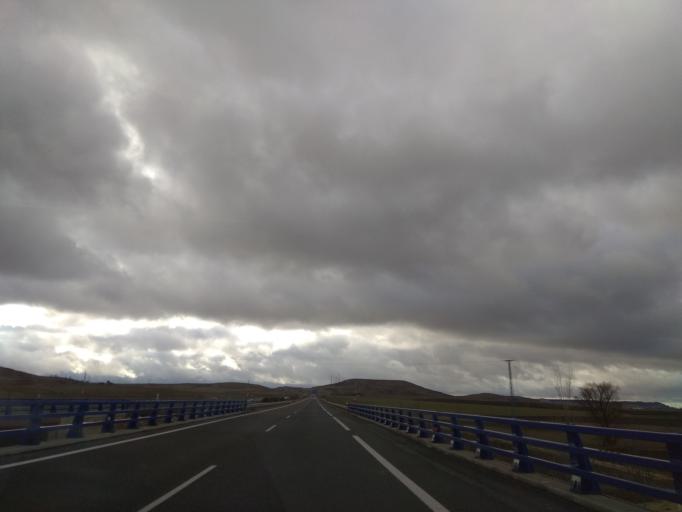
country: ES
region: Castille and Leon
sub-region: Provincia de Burgos
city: Sotragero
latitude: 42.4102
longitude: -3.6974
